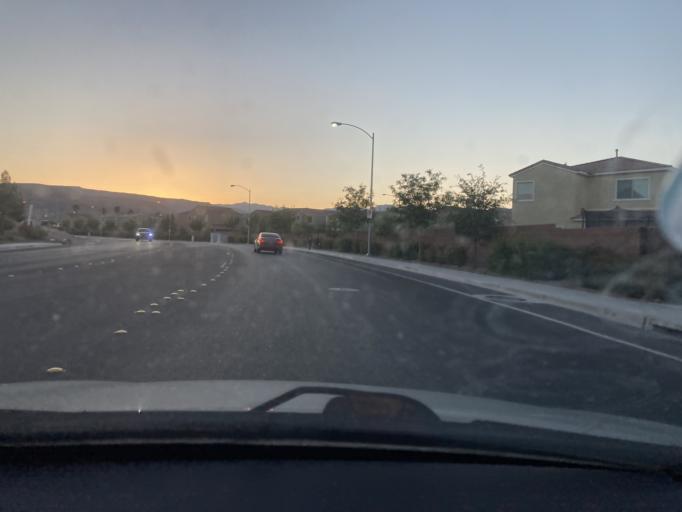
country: US
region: Nevada
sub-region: Clark County
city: Enterprise
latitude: 36.0626
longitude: -115.2867
